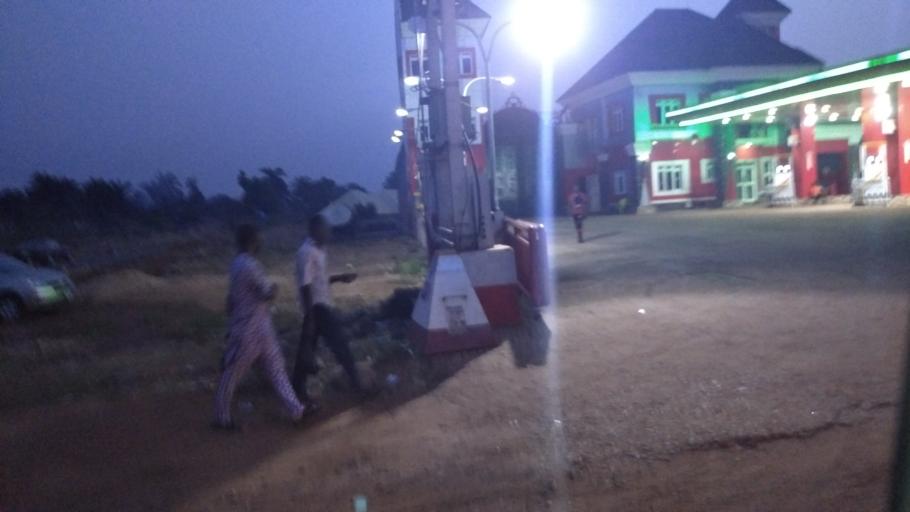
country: NG
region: Enugu
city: Enugu
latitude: 6.4664
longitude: 7.5962
